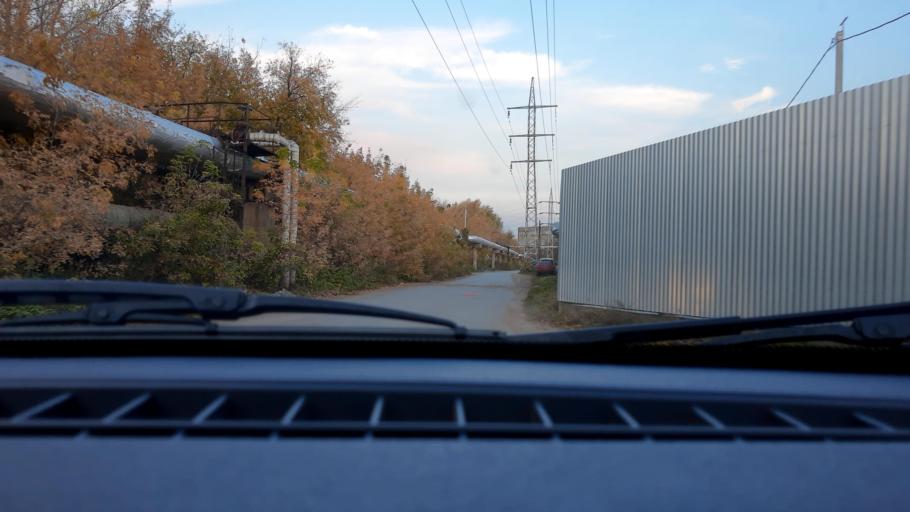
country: RU
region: Bashkortostan
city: Ufa
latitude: 54.7965
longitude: 56.1151
